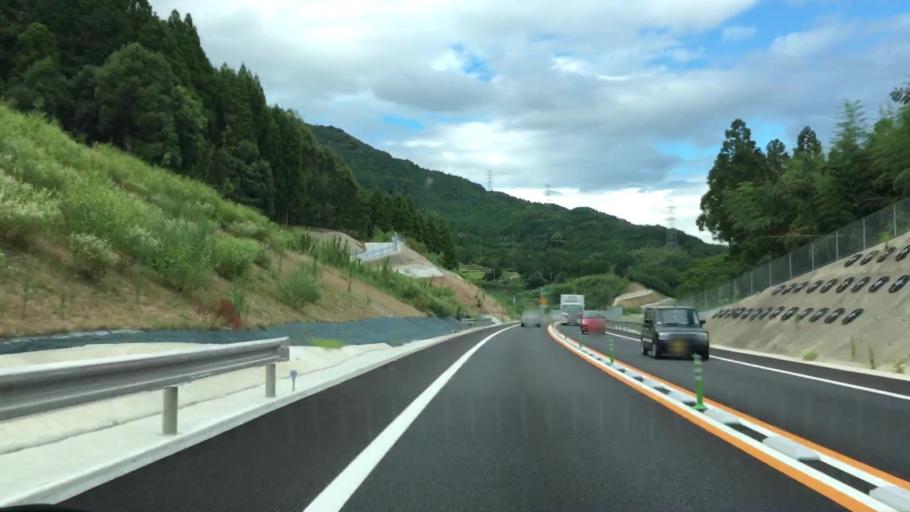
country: JP
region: Saga Prefecture
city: Imaricho-ko
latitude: 33.3091
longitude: 129.9166
